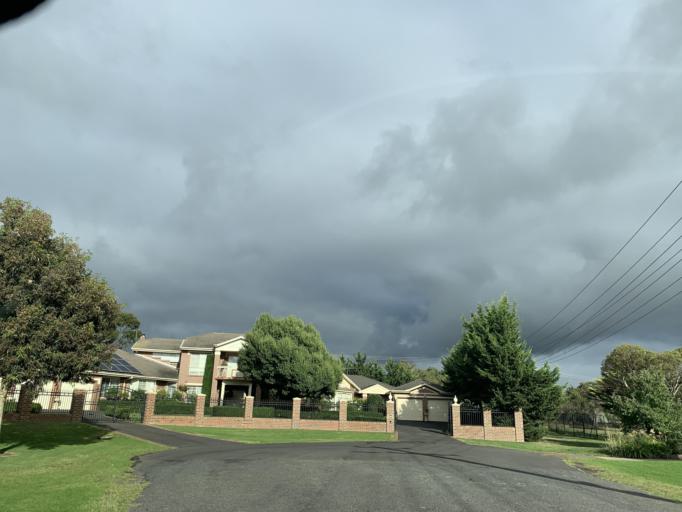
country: AU
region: Victoria
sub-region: Hume
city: Attwood
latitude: -37.6597
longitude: 144.8855
